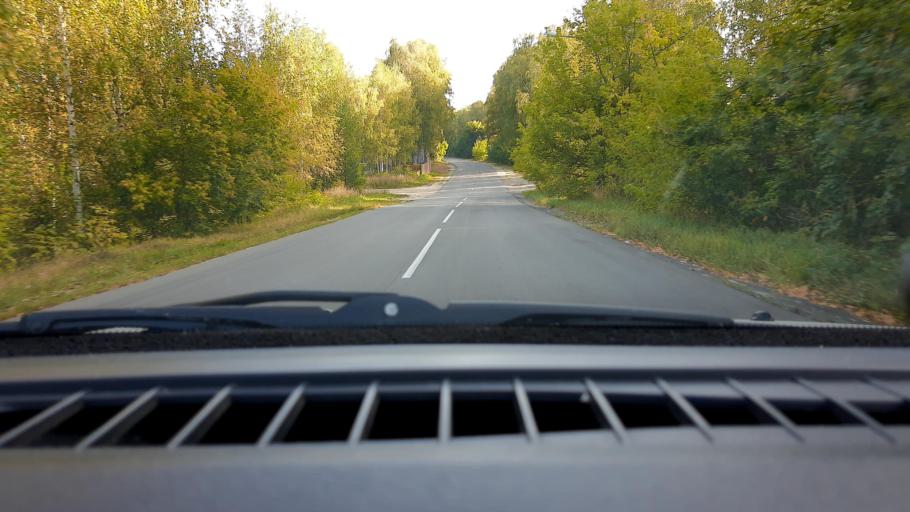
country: RU
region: Nizjnij Novgorod
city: Sitniki
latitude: 56.4707
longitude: 44.0377
